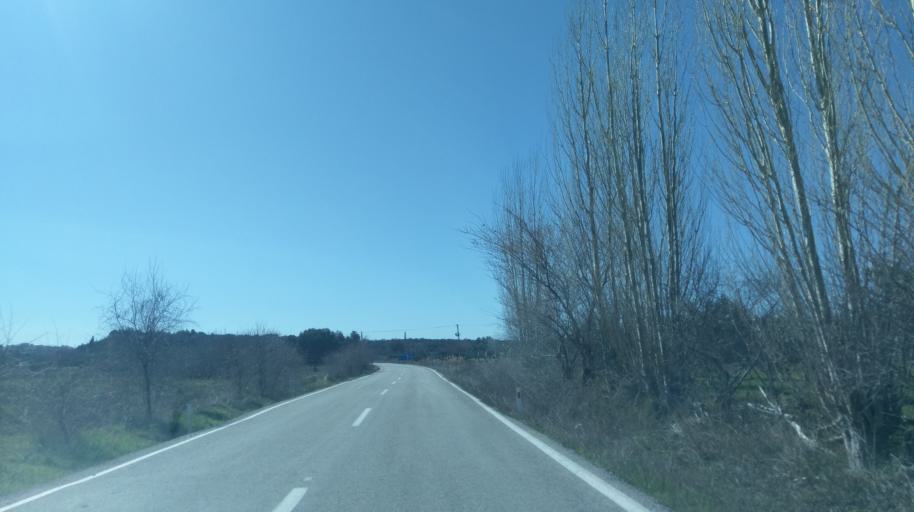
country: TR
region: Canakkale
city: Intepe
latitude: 40.0586
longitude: 26.2003
